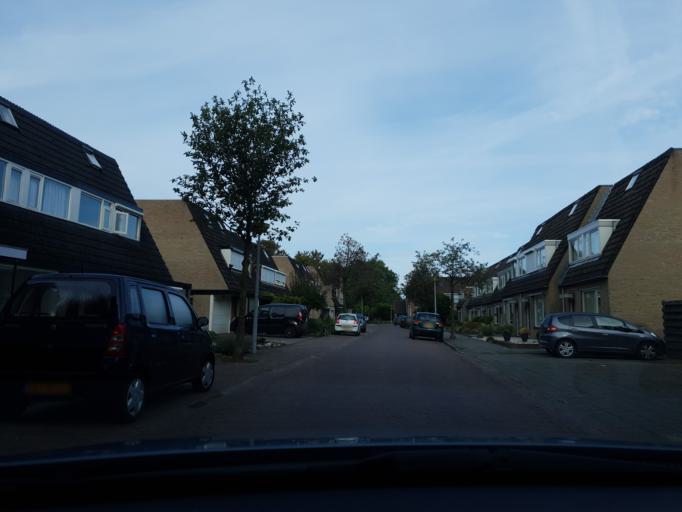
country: NL
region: Gelderland
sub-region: Gemeente Overbetuwe
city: Oosterhout
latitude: 51.8571
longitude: 5.8098
